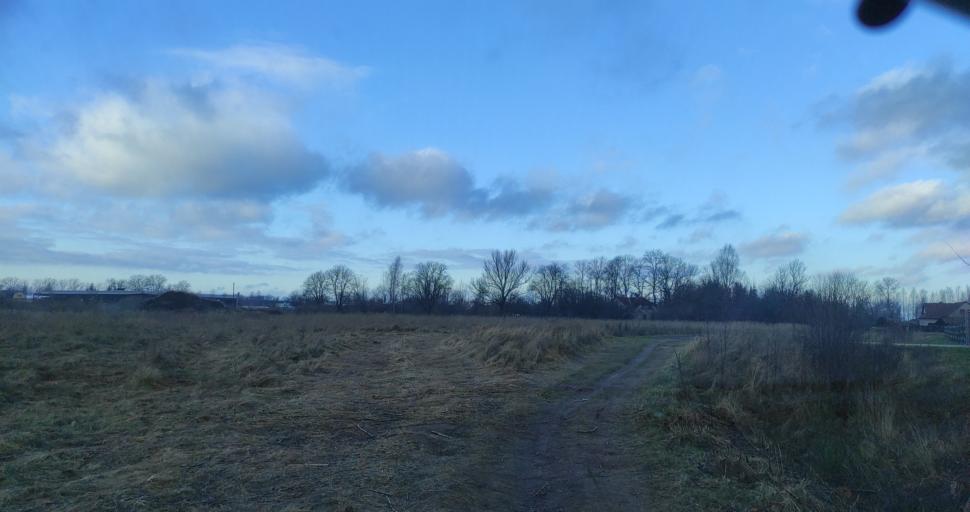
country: LV
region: Kuldigas Rajons
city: Kuldiga
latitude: 56.9566
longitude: 21.9980
